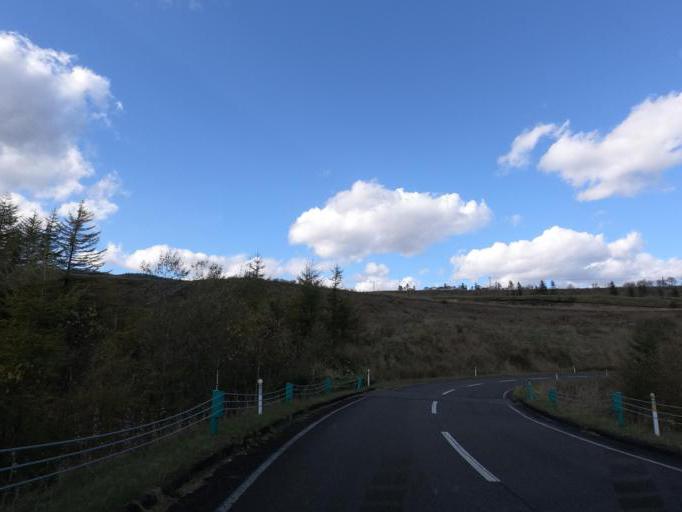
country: JP
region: Hokkaido
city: Otofuke
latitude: 43.2924
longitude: 143.1911
